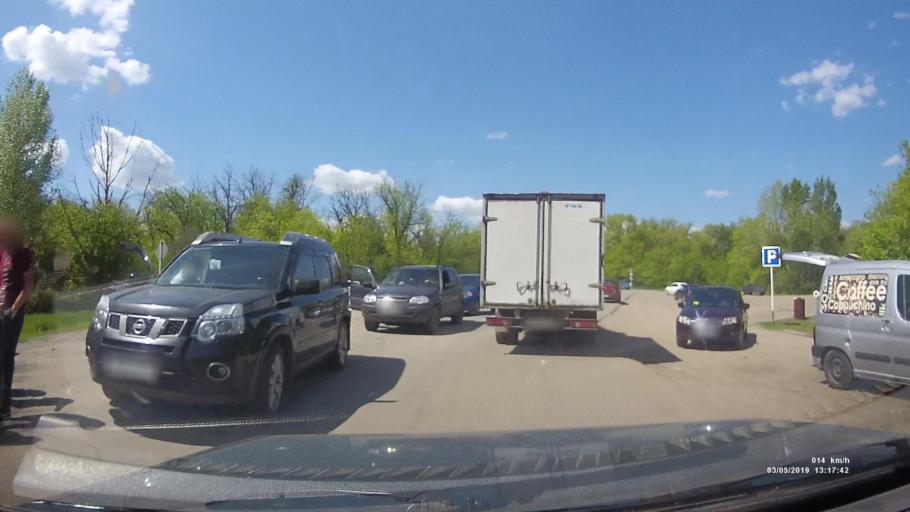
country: RU
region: Rostov
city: Semikarakorsk
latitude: 47.5302
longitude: 40.7509
